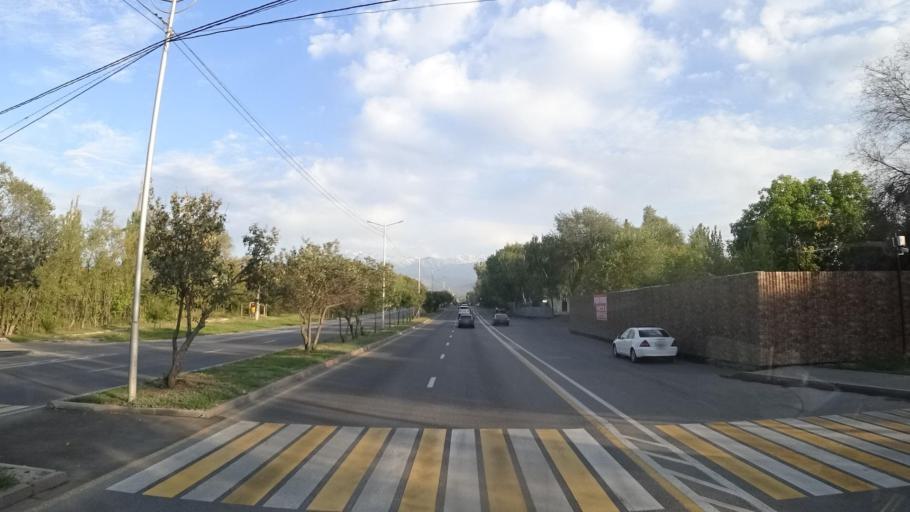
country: KZ
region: Almaty Oblysy
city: Pervomayskiy
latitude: 43.3399
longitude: 76.9983
